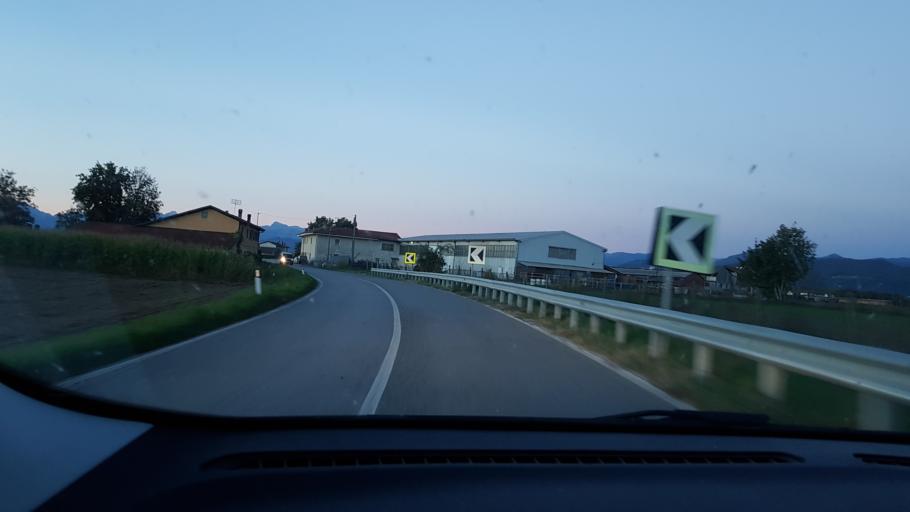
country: IT
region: Piedmont
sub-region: Provincia di Cuneo
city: Vottignasco
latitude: 44.5596
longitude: 7.5666
